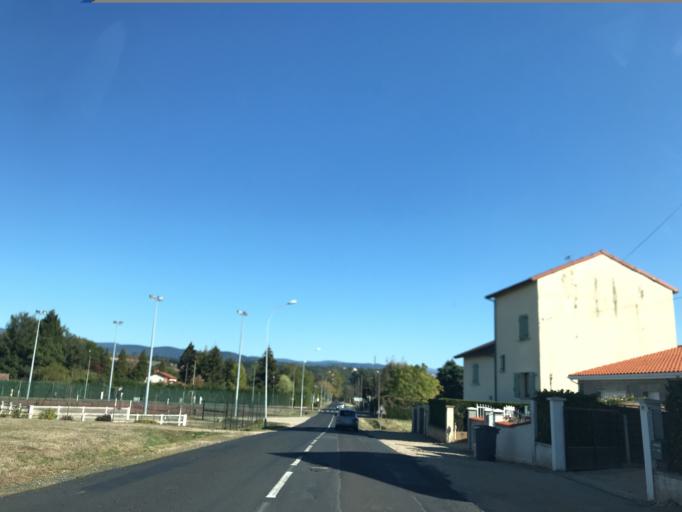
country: FR
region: Auvergne
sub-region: Departement du Puy-de-Dome
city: Courpiere
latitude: 45.7662
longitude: 3.5336
